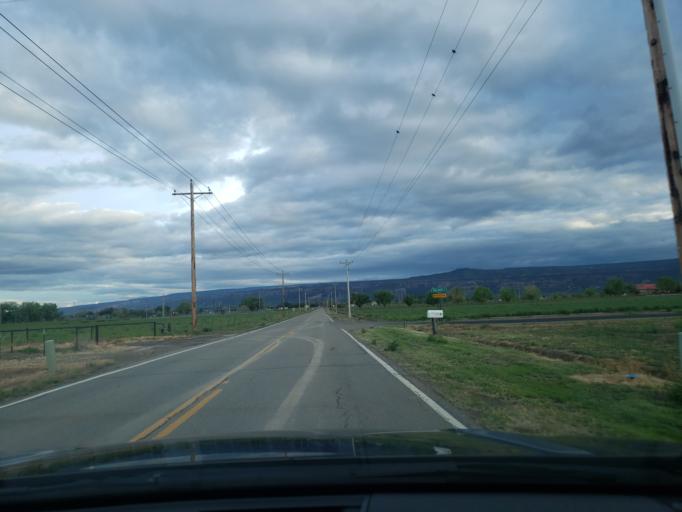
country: US
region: Colorado
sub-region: Mesa County
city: Fruita
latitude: 39.1900
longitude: -108.7013
